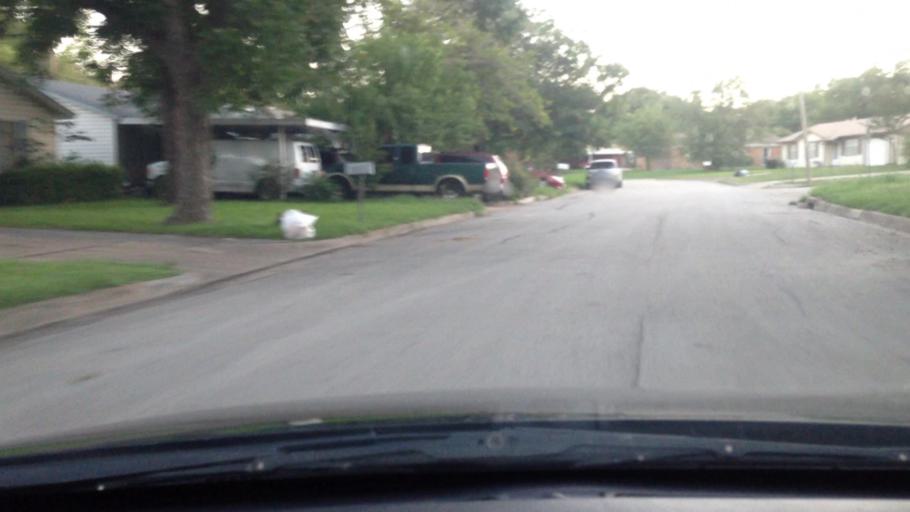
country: US
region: Texas
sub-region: Tarrant County
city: White Settlement
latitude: 32.7766
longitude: -97.4659
